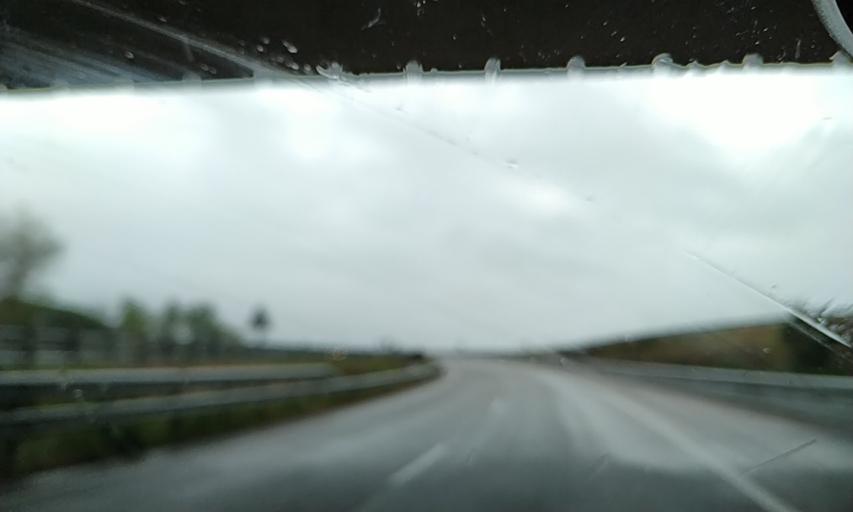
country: ES
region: Extremadura
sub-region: Provincia de Badajoz
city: Badajoz
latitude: 38.9168
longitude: -6.9615
